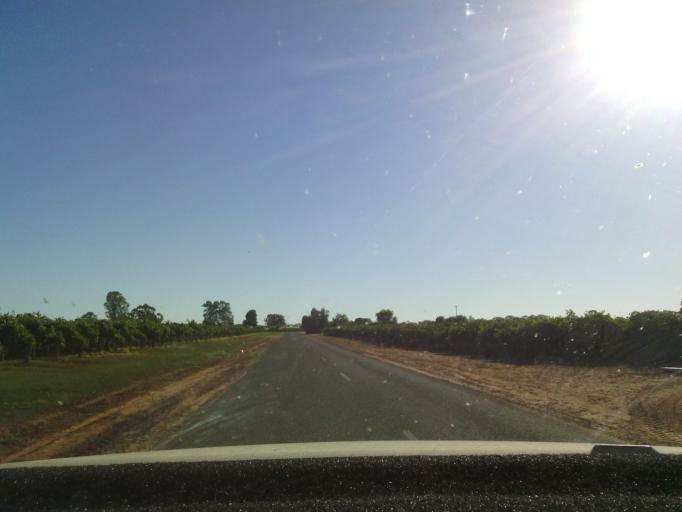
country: AU
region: South Australia
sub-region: Berri and Barmera
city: Monash
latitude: -34.2349
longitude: 140.5650
